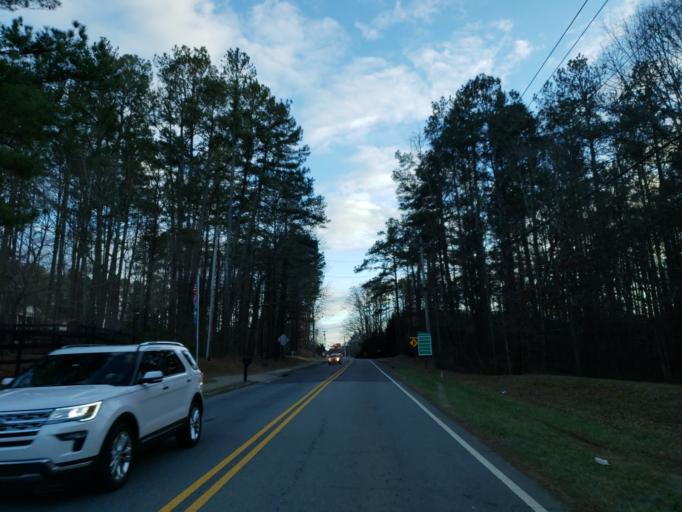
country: US
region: Georgia
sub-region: Cobb County
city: Kennesaw
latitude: 34.0010
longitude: -84.6760
